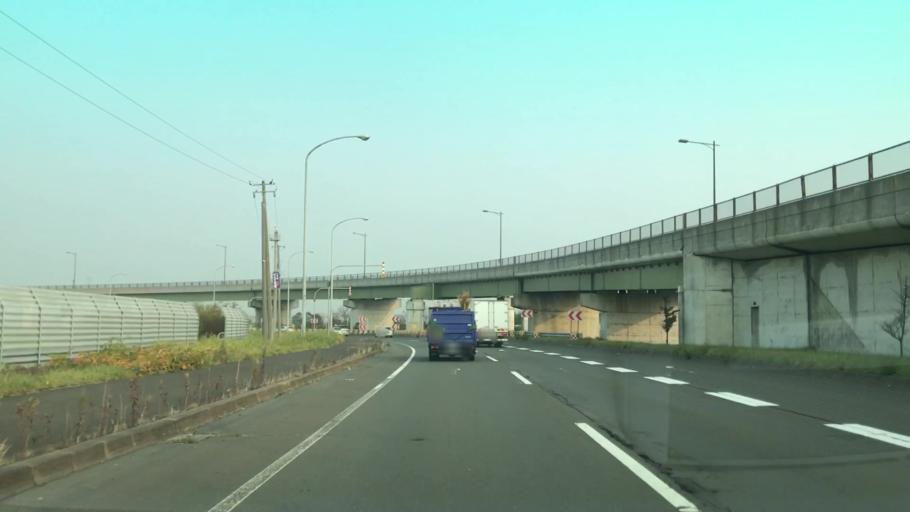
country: JP
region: Hokkaido
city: Ishikari
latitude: 43.1782
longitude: 141.3478
